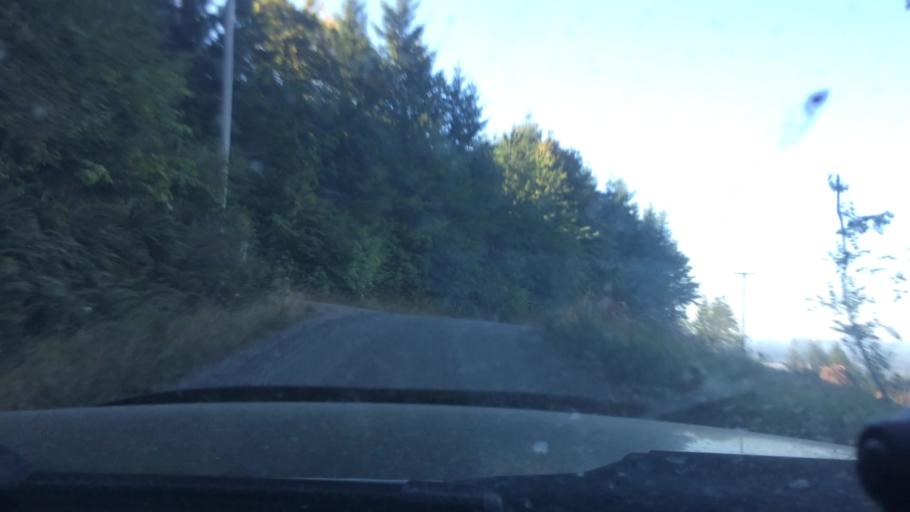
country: US
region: Oregon
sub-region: Yamhill County
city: Newberg
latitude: 45.3636
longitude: -122.9826
